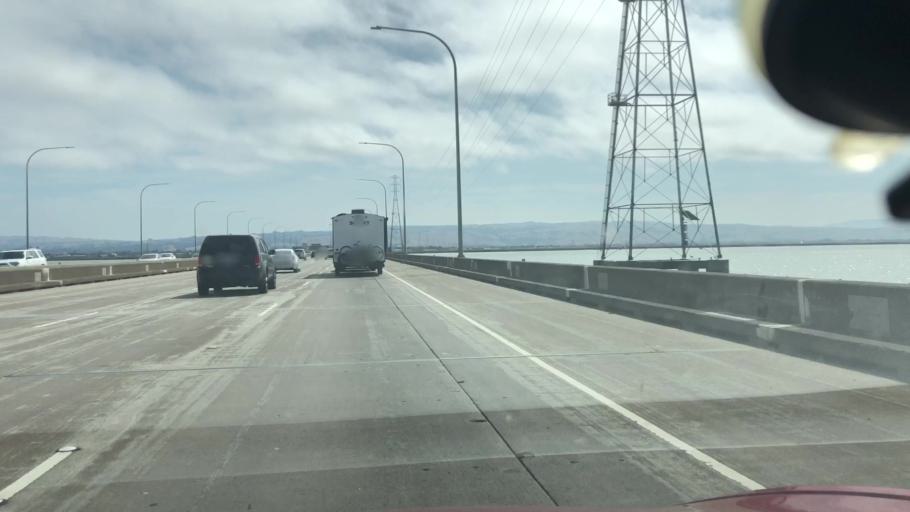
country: US
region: California
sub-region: Alameda County
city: San Lorenzo
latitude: 37.6144
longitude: -122.1620
